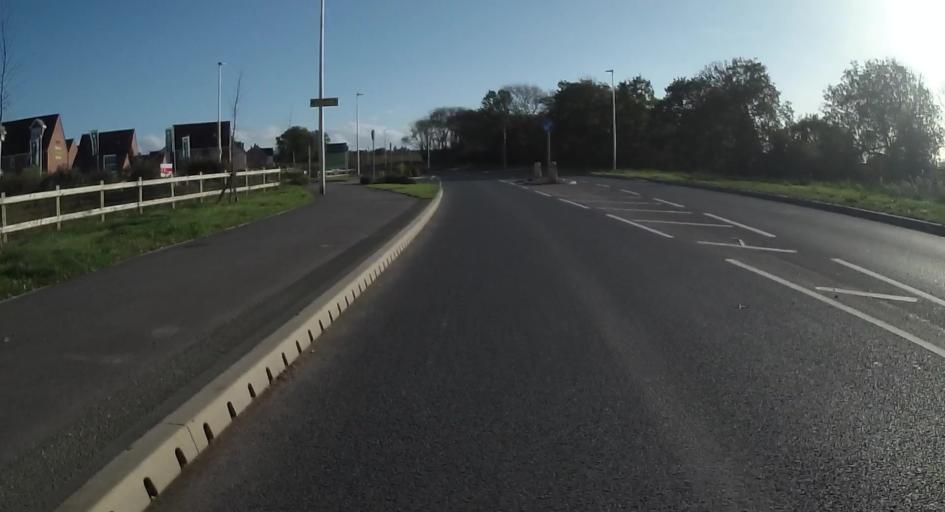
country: GB
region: England
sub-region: Wokingham
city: Winnersh
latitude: 51.4291
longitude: -0.8918
